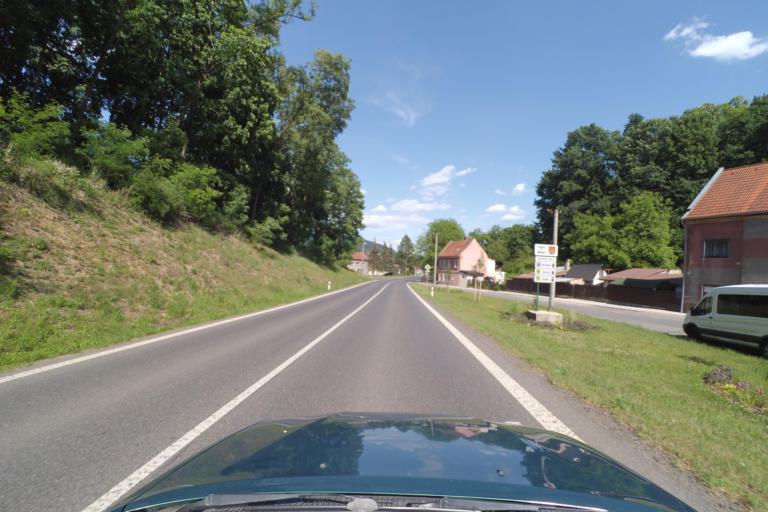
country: CZ
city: Mimon
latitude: 50.6605
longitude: 14.7216
